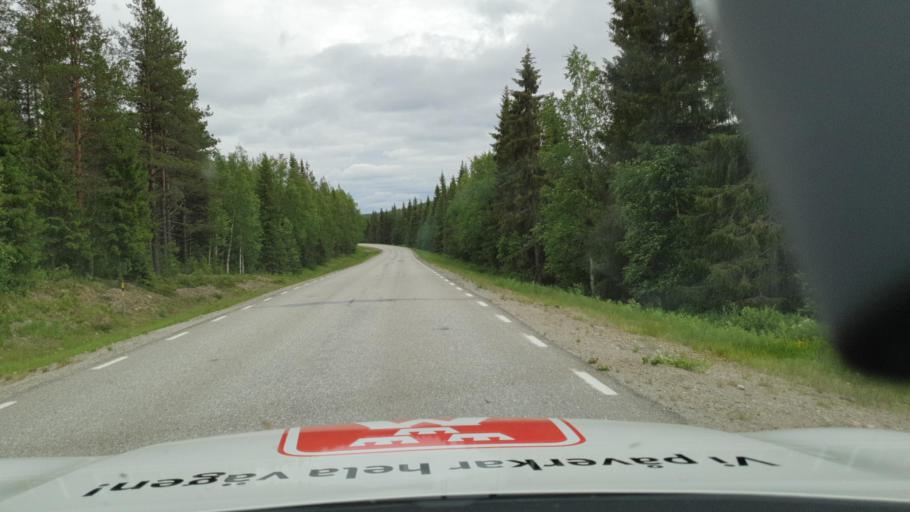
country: SE
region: Vaesterbotten
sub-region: Lycksele Kommun
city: Soderfors
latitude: 64.3186
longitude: 18.1570
